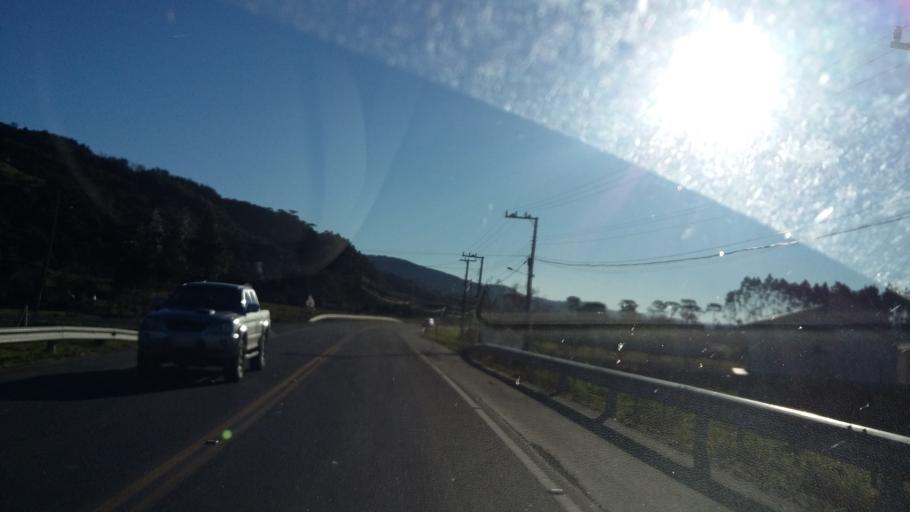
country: BR
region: Santa Catarina
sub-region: Lauro Muller
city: Lauro Muller
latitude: -27.9963
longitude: -49.5604
